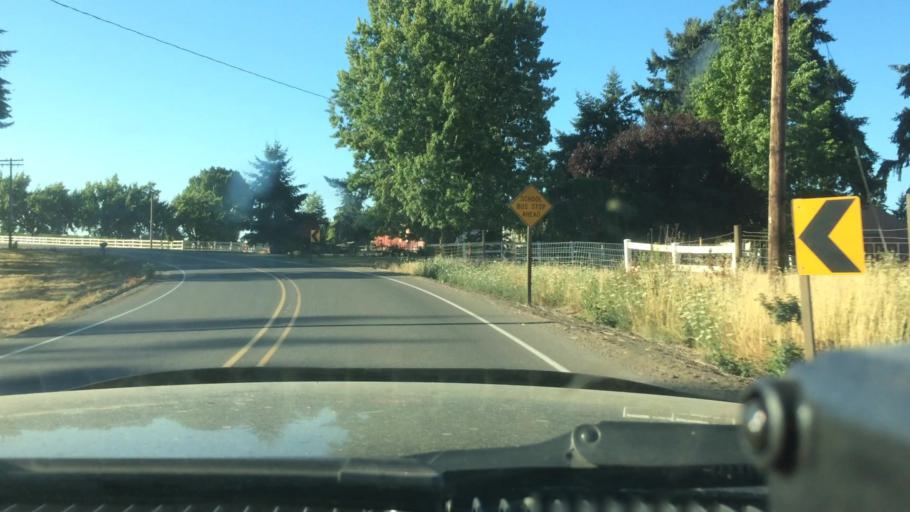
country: US
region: Oregon
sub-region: Marion County
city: Gervais
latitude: 45.1181
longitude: -122.9827
